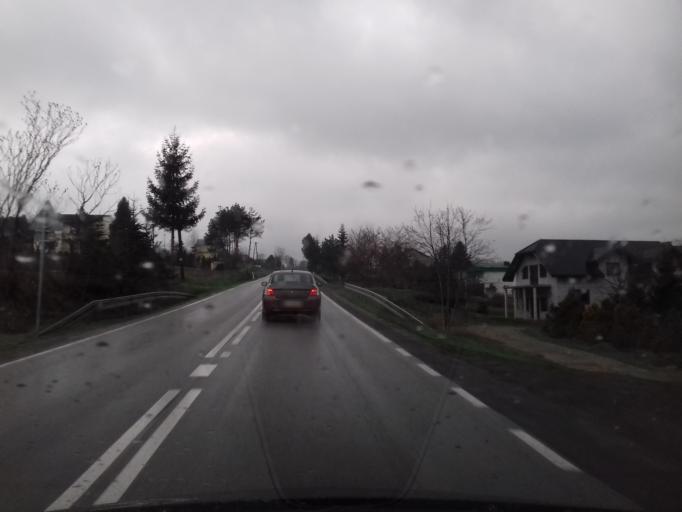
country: PL
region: Lesser Poland Voivodeship
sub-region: Powiat nowosadecki
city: Chelmiec
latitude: 49.6329
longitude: 20.6379
